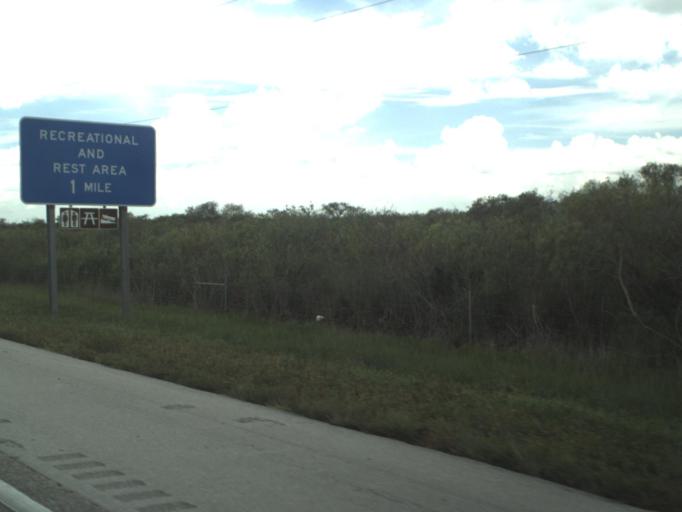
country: US
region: Florida
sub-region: Broward County
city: Weston
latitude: 26.1463
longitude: -80.6587
